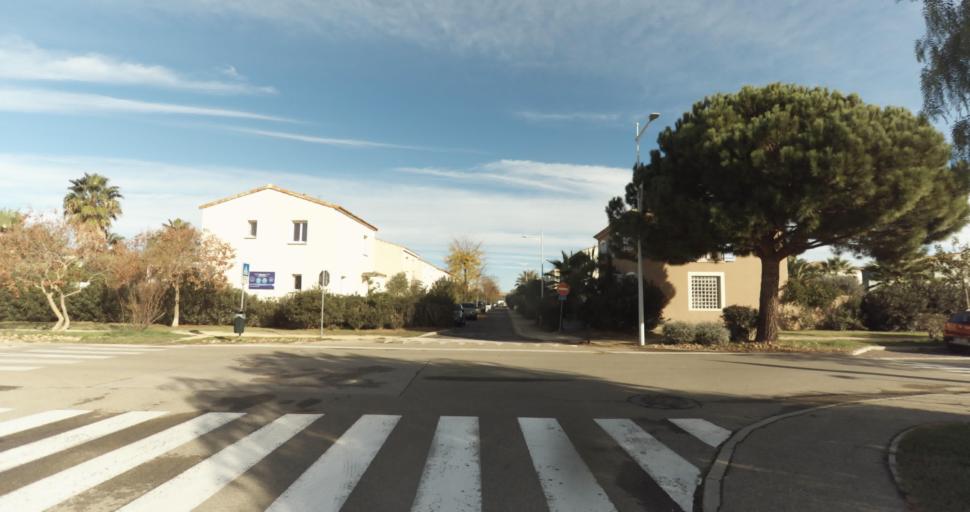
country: FR
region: Languedoc-Roussillon
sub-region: Departement du Gard
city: Aigues-Mortes
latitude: 43.5733
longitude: 4.1821
